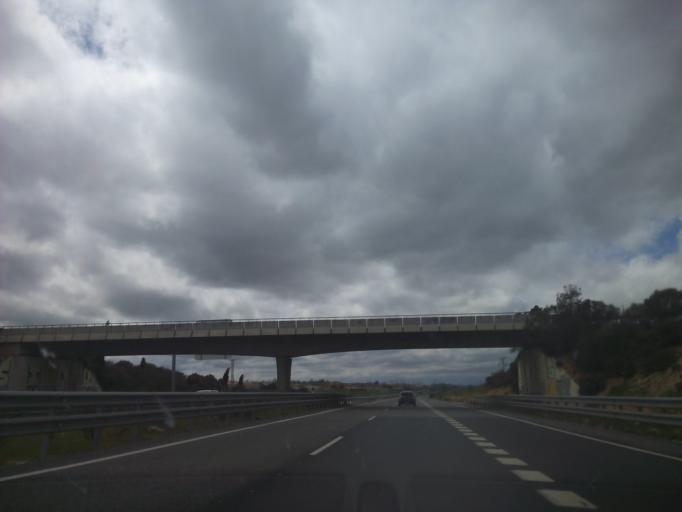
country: ES
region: Castille and Leon
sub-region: Provincia de Salamanca
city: Santa Marta de Tormes
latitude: 40.9447
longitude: -5.6067
